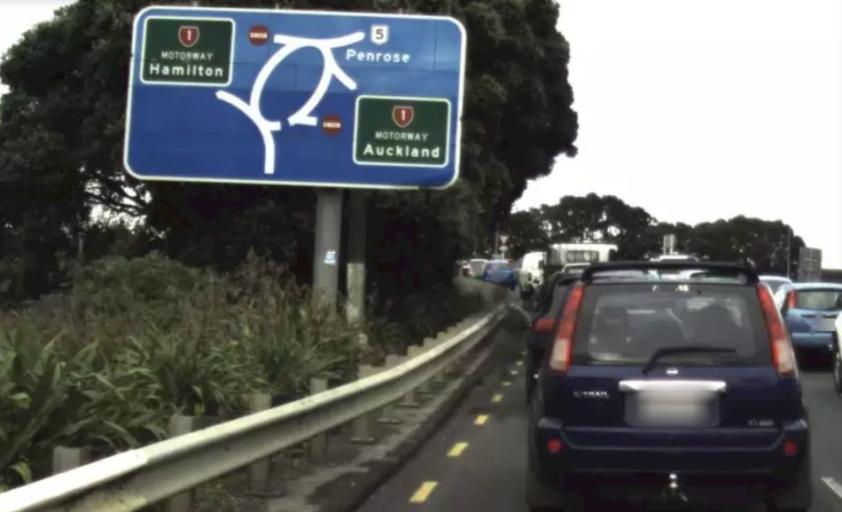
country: NZ
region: Auckland
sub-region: Auckland
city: Tamaki
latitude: -36.9022
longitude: 174.8125
